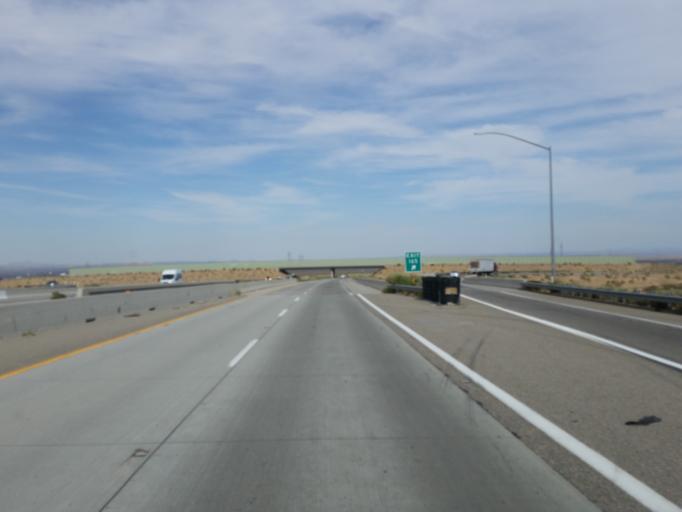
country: US
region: California
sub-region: Kern County
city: Mojave
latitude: 35.1148
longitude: -118.1844
